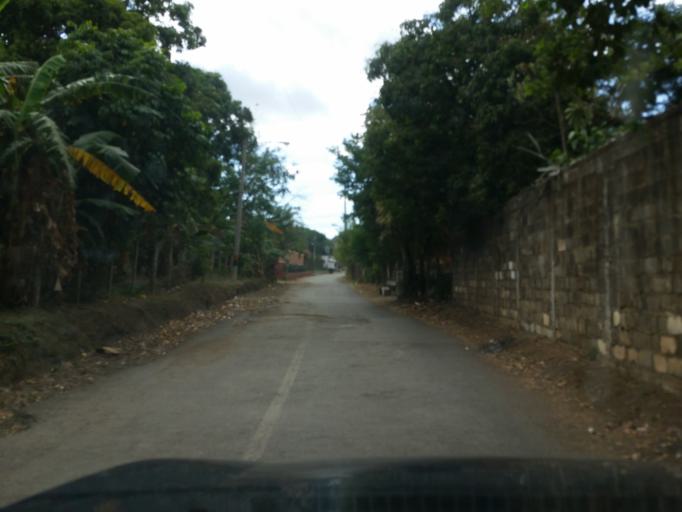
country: NI
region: Masaya
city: Ticuantepe
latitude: 12.0735
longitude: -86.2217
